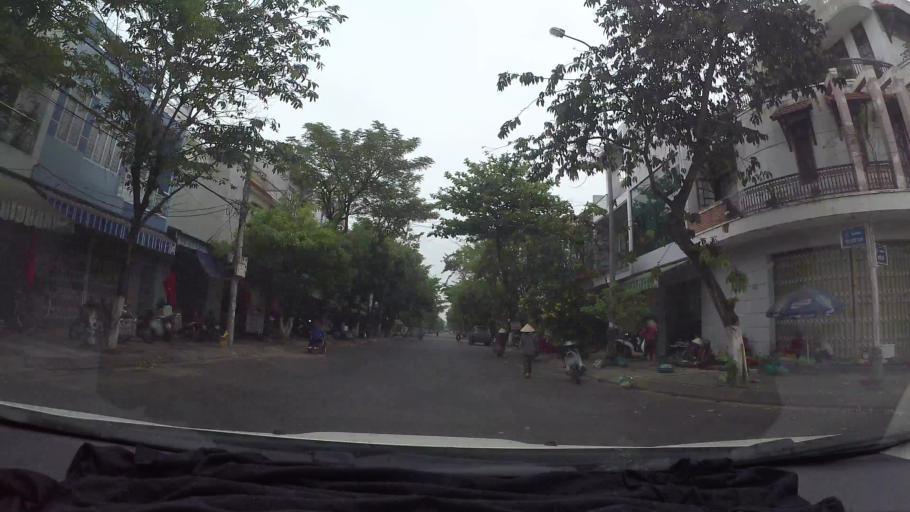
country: VN
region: Da Nang
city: Cam Le
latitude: 16.0228
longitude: 108.2131
